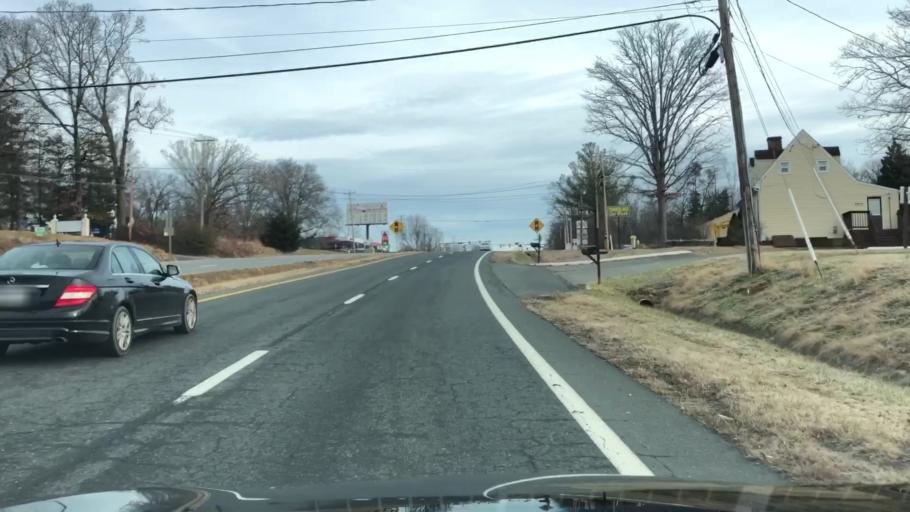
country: US
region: Virginia
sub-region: Campbell County
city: Timberlake
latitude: 37.3158
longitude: -79.2619
